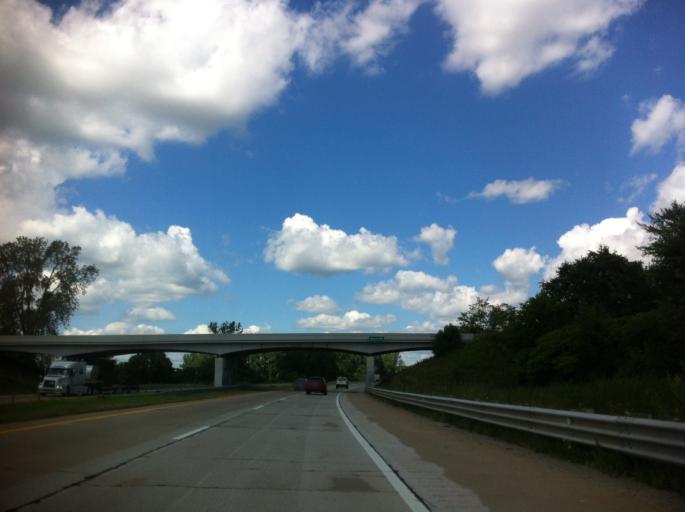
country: US
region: Michigan
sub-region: Monroe County
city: Lambertville
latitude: 41.8213
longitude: -83.6842
